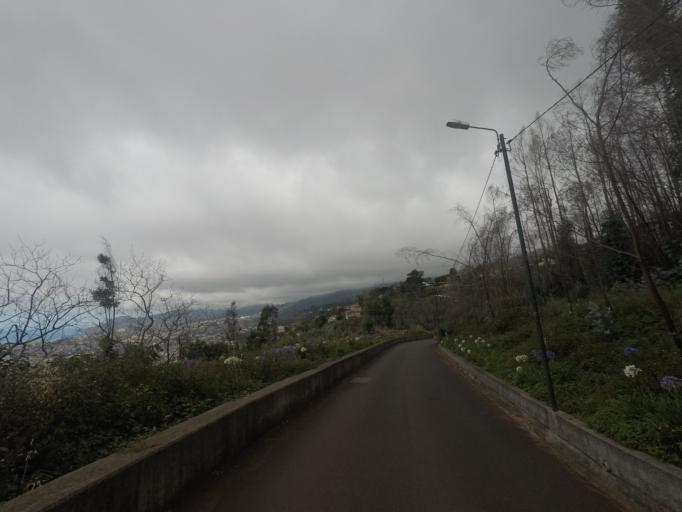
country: PT
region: Madeira
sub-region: Funchal
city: Nossa Senhora do Monte
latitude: 32.6664
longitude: -16.8871
